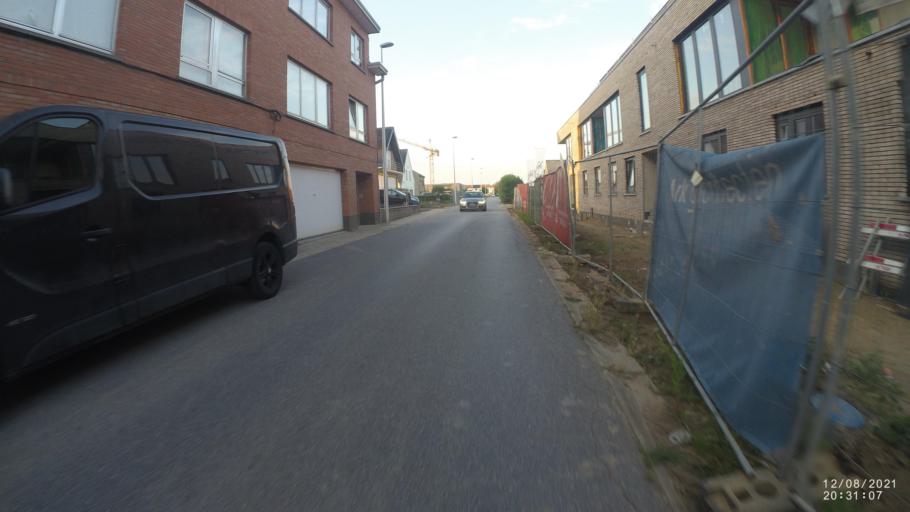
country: BE
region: Flanders
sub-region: Provincie Vlaams-Brabant
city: Dilbeek
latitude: 50.8613
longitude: 4.2613
